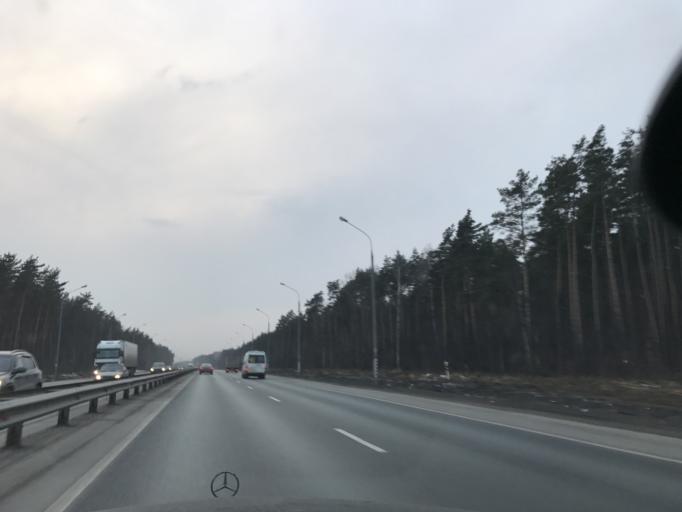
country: RU
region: Moskovskaya
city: Monino
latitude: 55.8261
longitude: 38.2277
